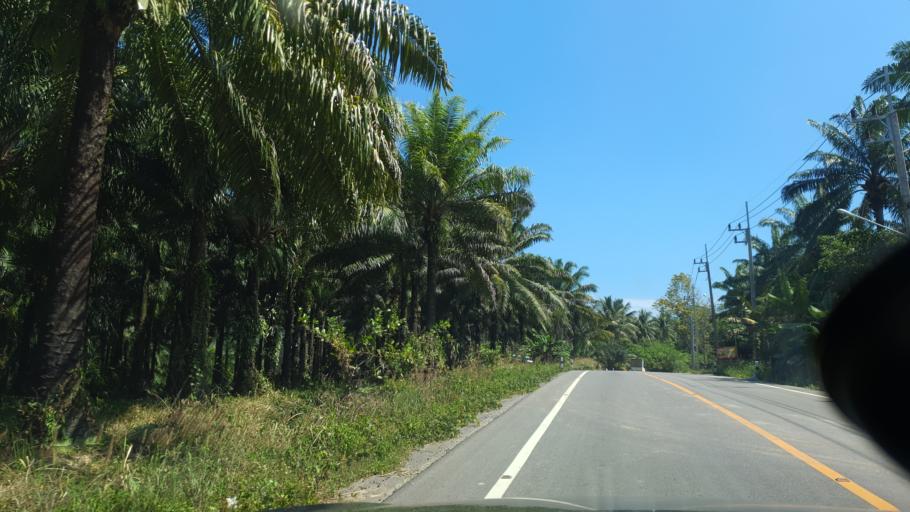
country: TH
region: Krabi
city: Khlong Thom
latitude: 7.9289
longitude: 99.2327
